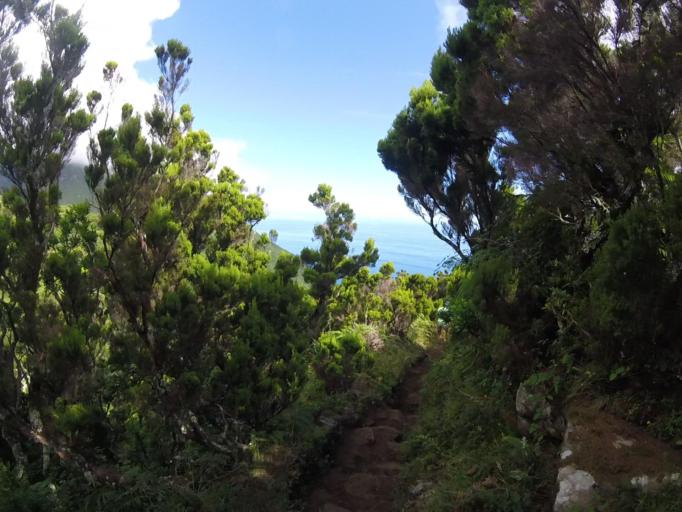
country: PT
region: Azores
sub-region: Sao Roque do Pico
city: Sao Roque do Pico
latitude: 38.6061
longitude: -27.9207
